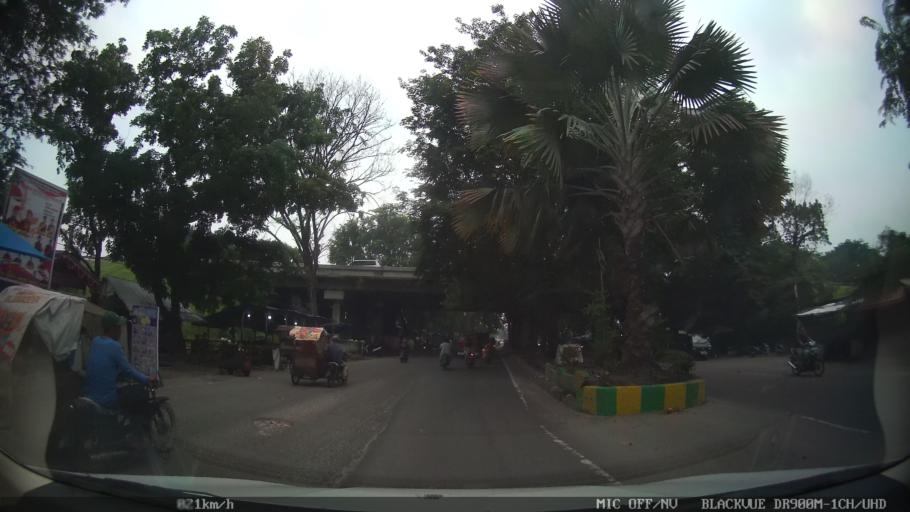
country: ID
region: North Sumatra
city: Medan
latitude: 3.5814
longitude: 98.7237
